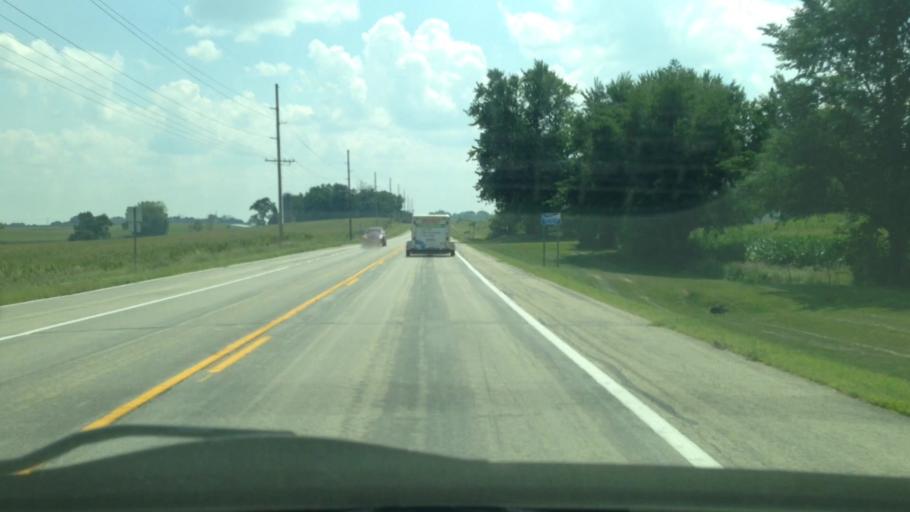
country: US
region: Minnesota
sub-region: Olmsted County
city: Rochester
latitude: 43.9416
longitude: -92.4087
